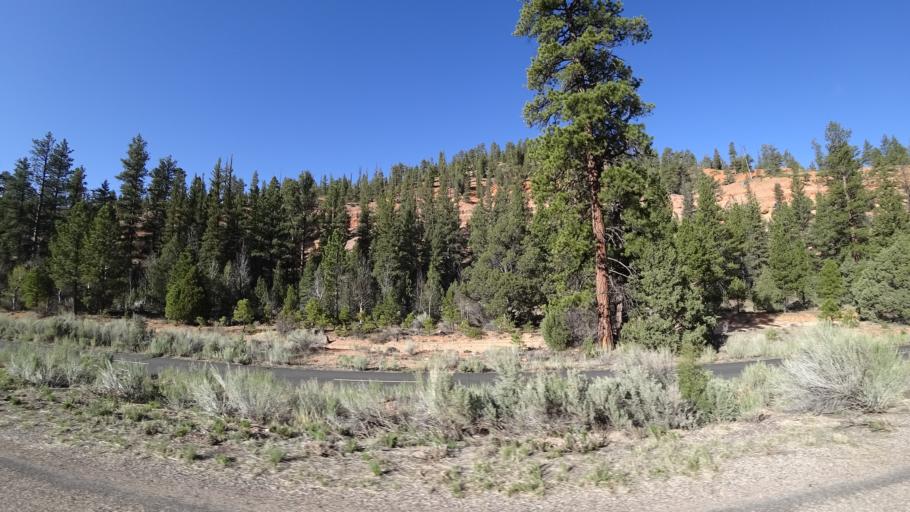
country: US
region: Utah
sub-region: Garfield County
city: Panguitch
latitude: 37.7388
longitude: -112.2948
